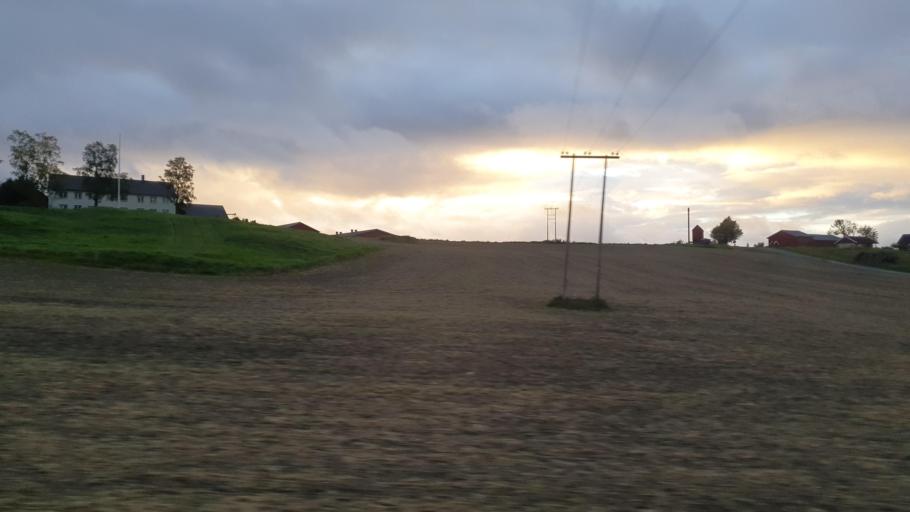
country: NO
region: Nord-Trondelag
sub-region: Levanger
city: Skogn
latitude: 63.6831
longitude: 11.1751
